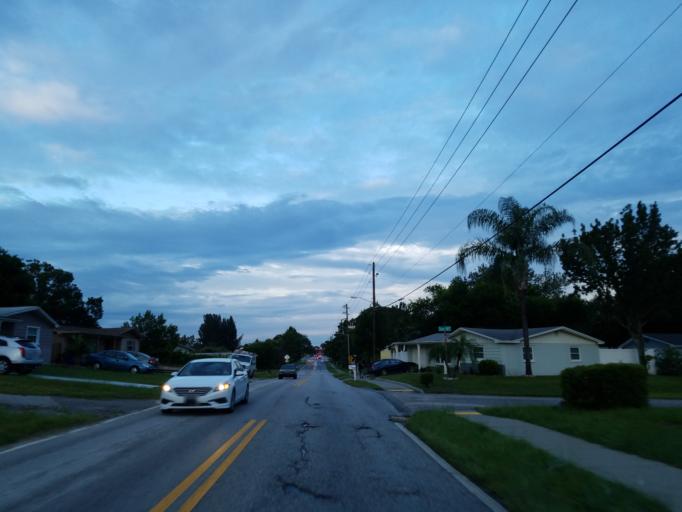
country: US
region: Florida
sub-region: Pasco County
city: Beacon Square
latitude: 28.2096
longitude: -82.7440
